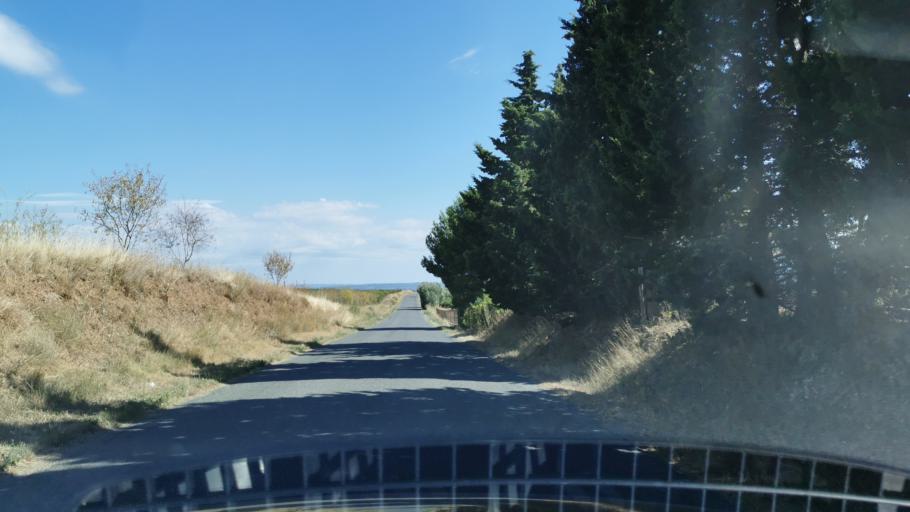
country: FR
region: Languedoc-Roussillon
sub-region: Departement de l'Aude
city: Caunes-Minervois
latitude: 43.3211
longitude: 2.5390
